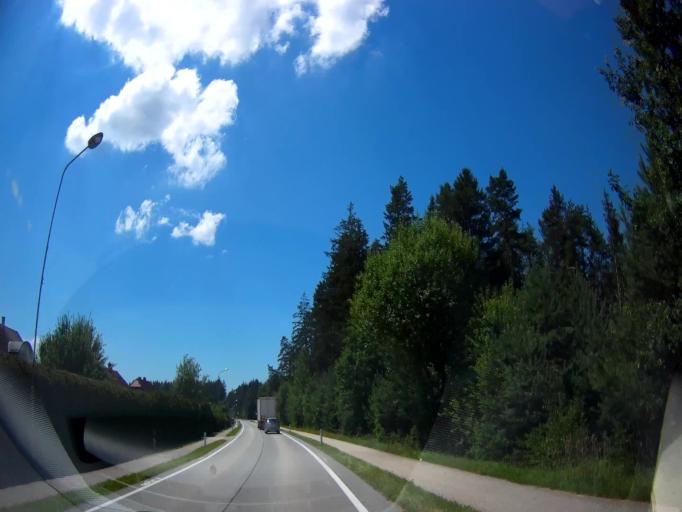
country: AT
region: Carinthia
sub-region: Politischer Bezirk Volkermarkt
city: Globasnitz
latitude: 46.6073
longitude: 14.7055
